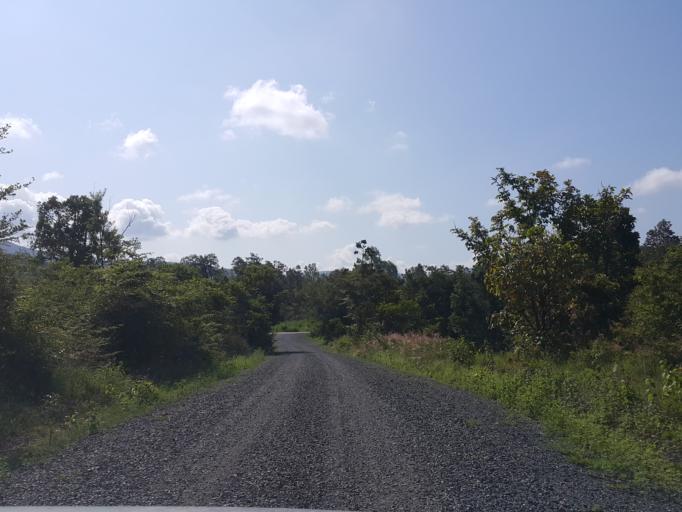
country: TH
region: Chiang Mai
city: Mae On
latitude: 18.8174
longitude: 99.1765
